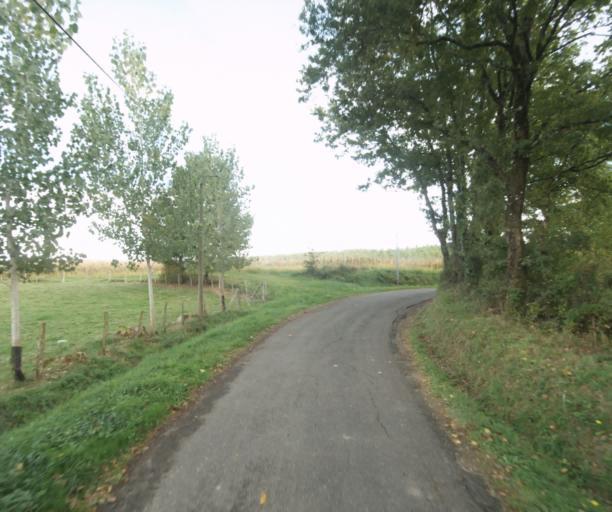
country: FR
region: Midi-Pyrenees
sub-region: Departement du Gers
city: Cazaubon
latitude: 43.8656
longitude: -0.1201
